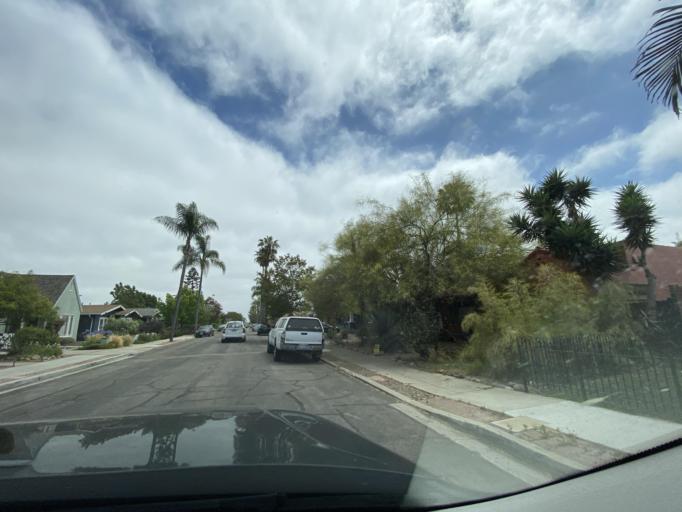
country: US
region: California
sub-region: San Diego County
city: San Diego
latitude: 32.7391
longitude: -117.1231
